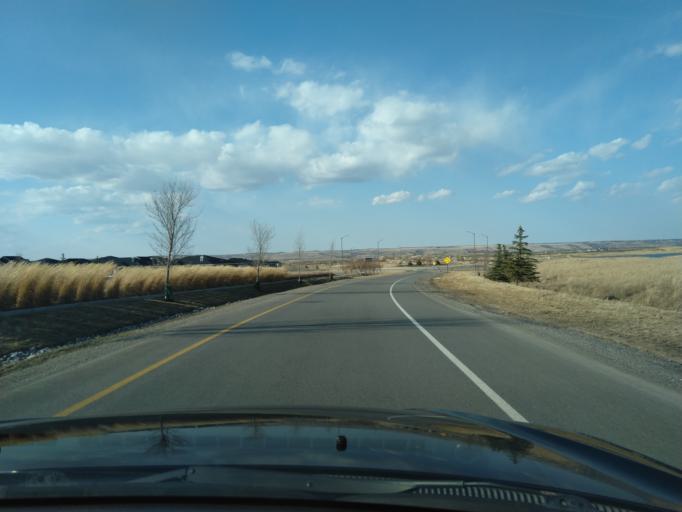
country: CA
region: Alberta
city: Cochrane
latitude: 51.1074
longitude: -114.3920
